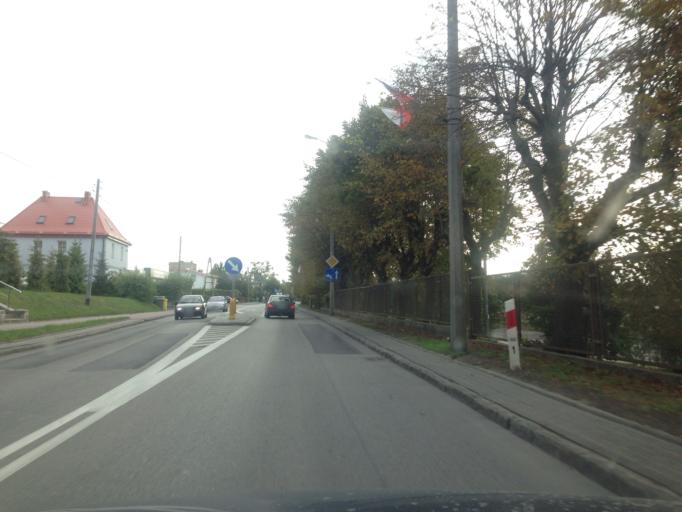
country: PL
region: Pomeranian Voivodeship
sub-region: Powiat kwidzynski
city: Kwidzyn
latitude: 53.7293
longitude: 18.9343
